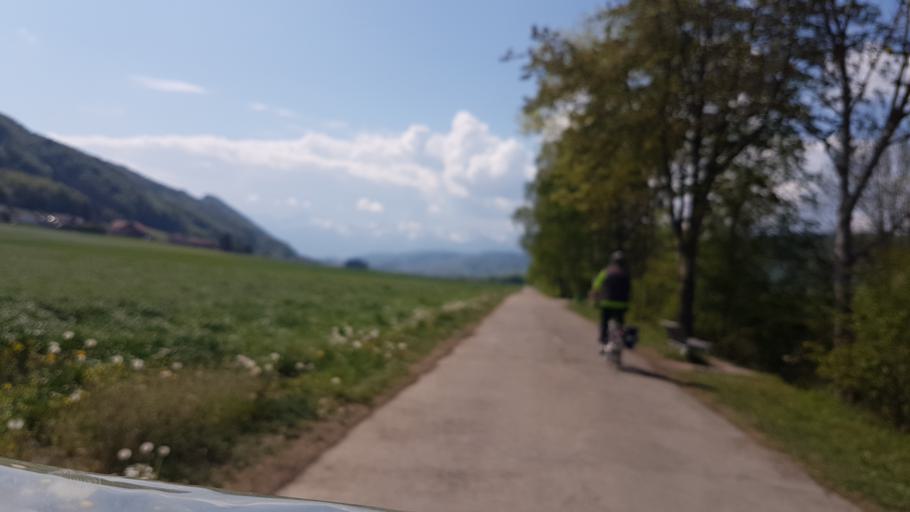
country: CH
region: Bern
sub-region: Bern-Mittelland District
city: Belp
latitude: 46.8823
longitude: 7.5011
